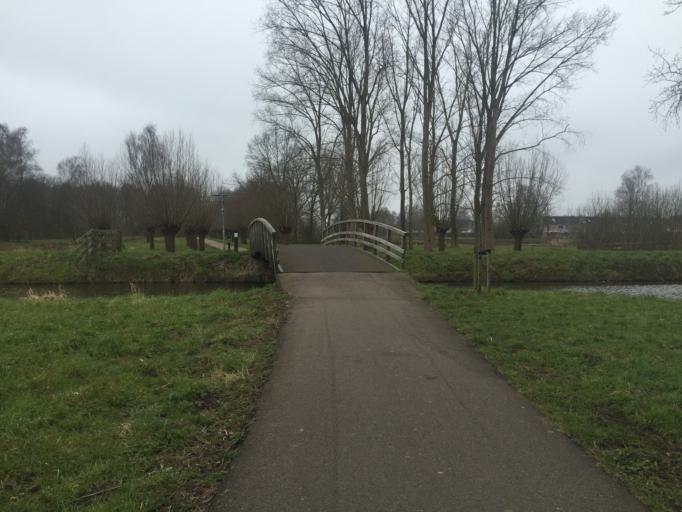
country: NL
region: South Holland
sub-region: Gemeente Vlist
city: Haastrecht
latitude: 52.0083
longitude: 4.7558
